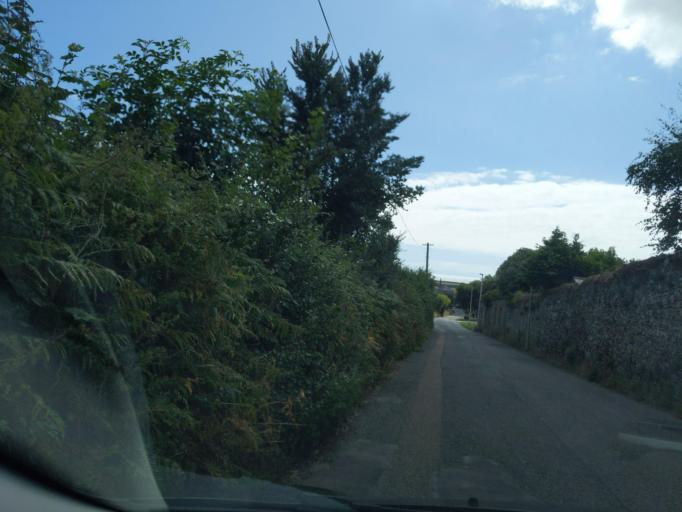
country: GB
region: England
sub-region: Devon
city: Modbury
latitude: 50.3539
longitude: -3.8879
